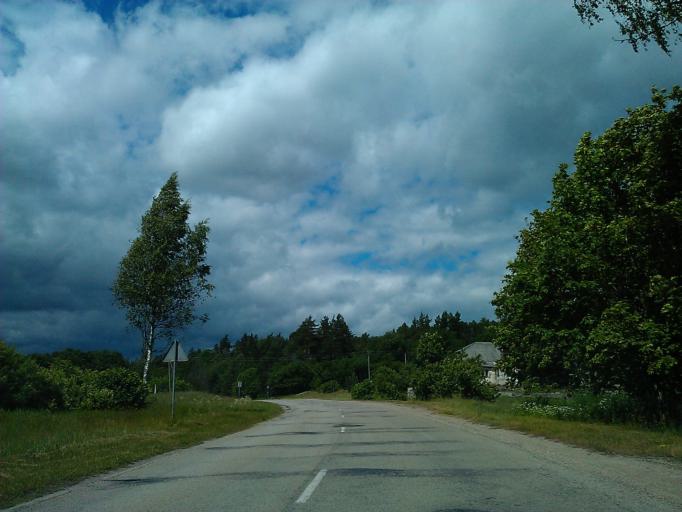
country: LV
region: Talsu Rajons
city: Sabile
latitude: 57.0850
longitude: 22.5236
